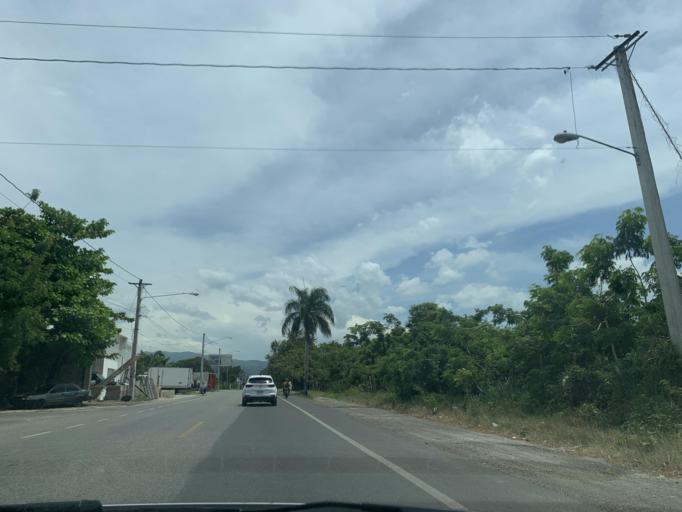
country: DO
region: Puerto Plata
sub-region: Puerto Plata
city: Puerto Plata
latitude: 19.7353
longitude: -70.6041
